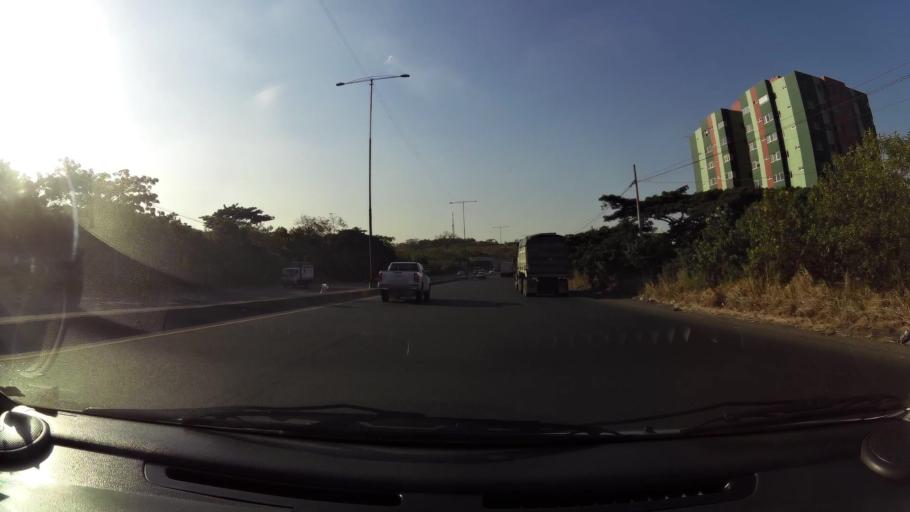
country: EC
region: Guayas
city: Santa Lucia
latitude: -2.1595
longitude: -79.9489
